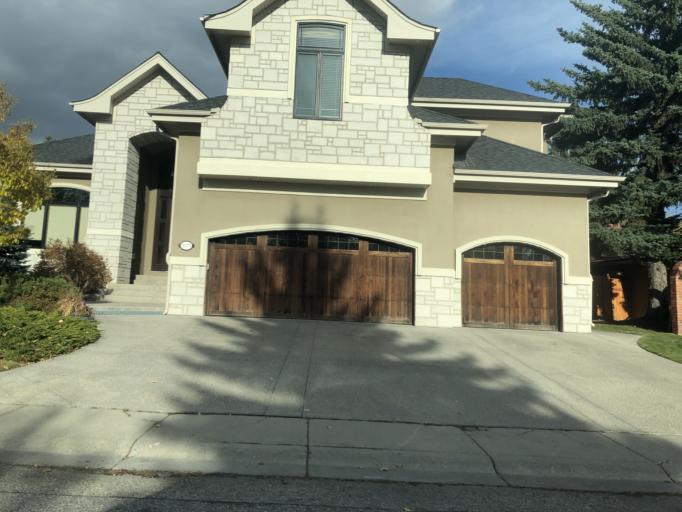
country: CA
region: Alberta
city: Calgary
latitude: 50.9312
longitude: -114.0590
